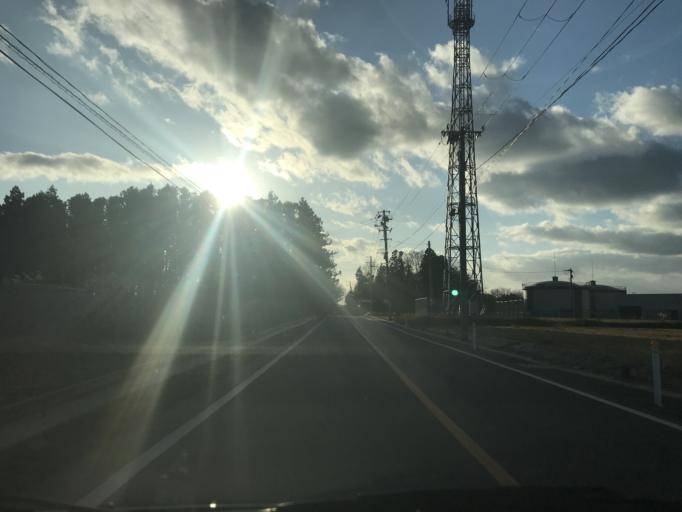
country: JP
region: Miyagi
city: Wakuya
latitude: 38.6712
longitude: 141.1047
